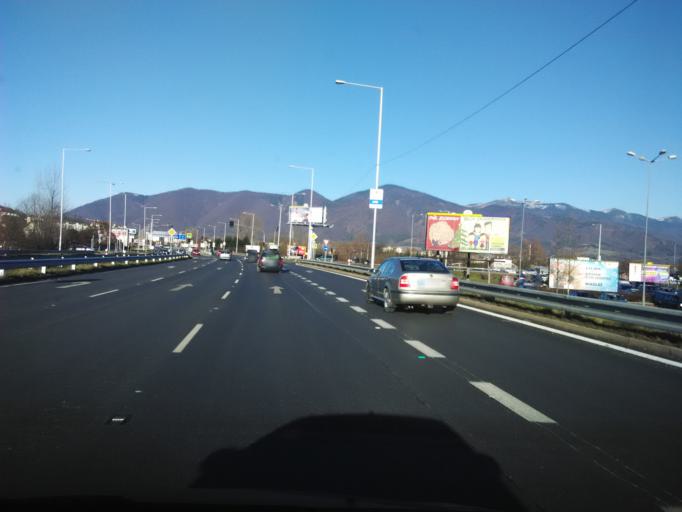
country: SK
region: Zilinsky
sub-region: Okres Martin
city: Martin
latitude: 49.0849
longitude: 18.9222
